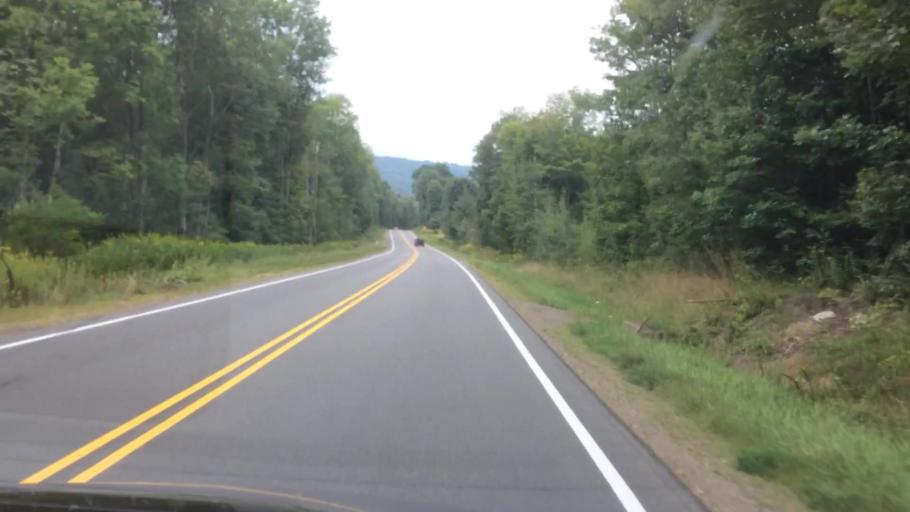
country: US
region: Pennsylvania
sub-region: McKean County
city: Bradford
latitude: 41.8843
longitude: -78.5826
